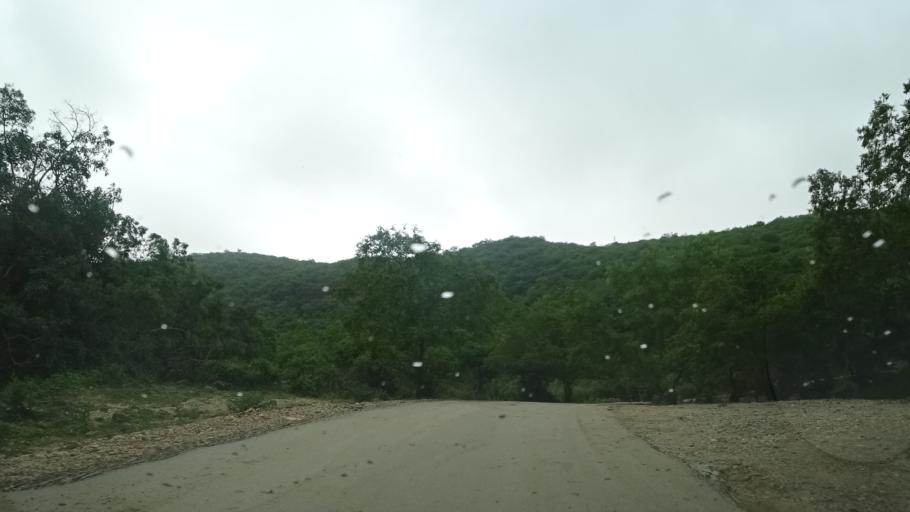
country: OM
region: Zufar
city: Salalah
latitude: 17.0985
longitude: 54.3262
